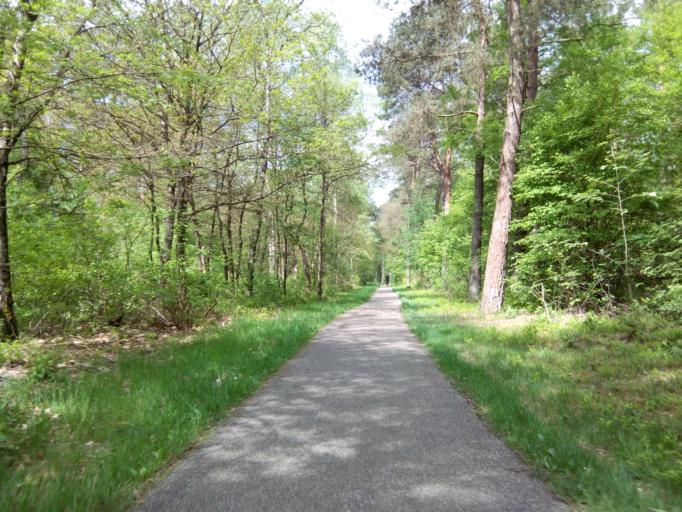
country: NL
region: Gelderland
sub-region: Gemeente Ede
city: Otterlo
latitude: 52.0893
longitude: 5.7568
